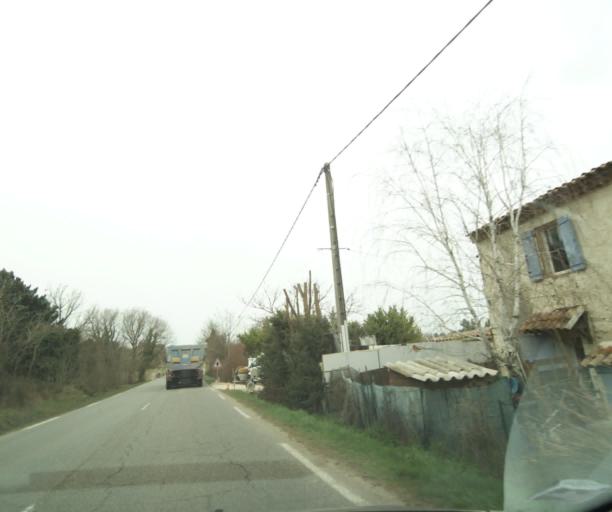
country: FR
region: Provence-Alpes-Cote d'Azur
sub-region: Departement des Bouches-du-Rhone
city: Peynier
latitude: 43.4472
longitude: 5.6544
